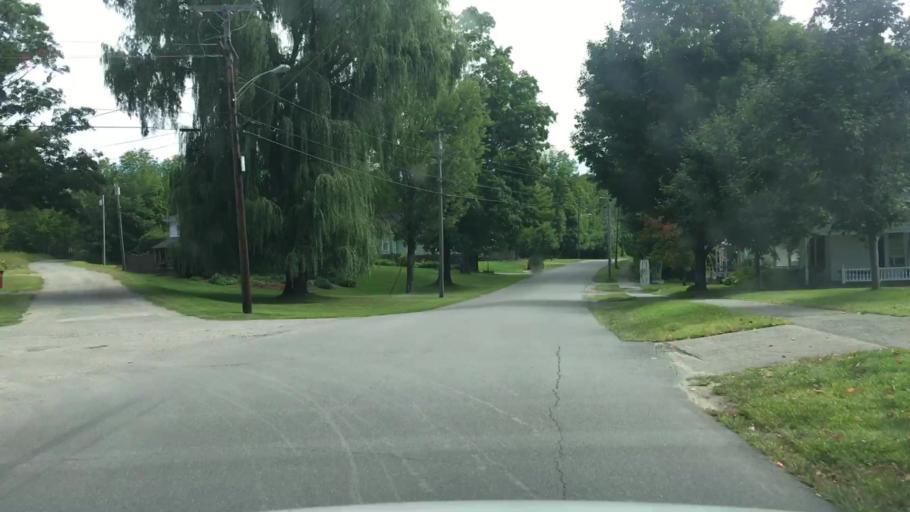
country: US
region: Maine
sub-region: Piscataquis County
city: Dover-Foxcroft
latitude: 45.1857
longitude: -69.2219
